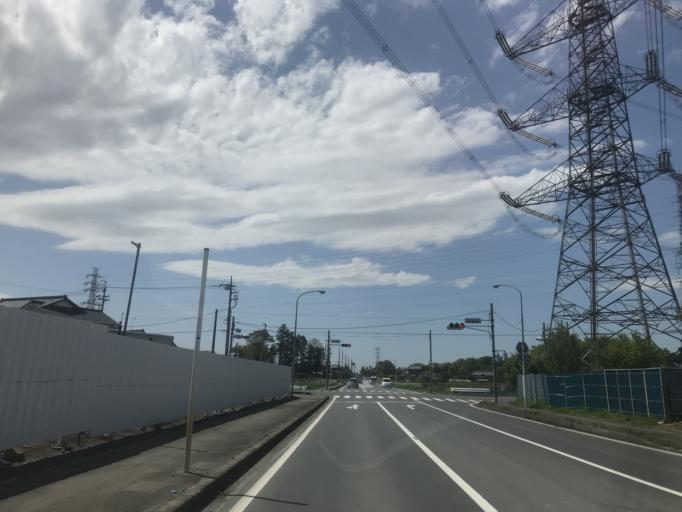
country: JP
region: Chiba
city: Noda
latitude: 35.9638
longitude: 139.9041
